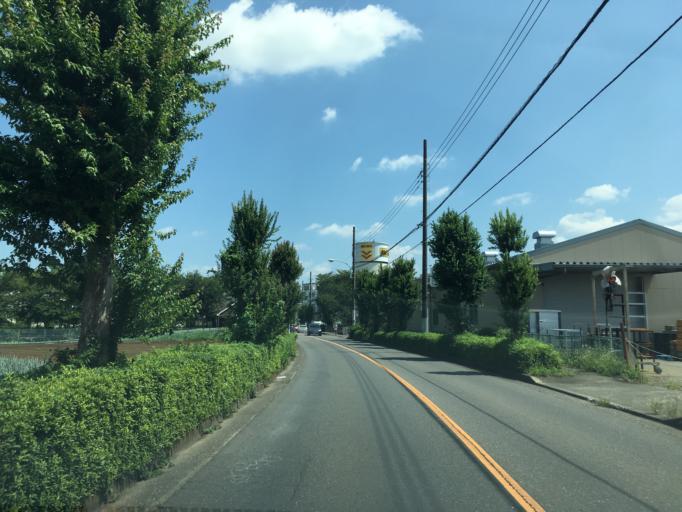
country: JP
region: Tokyo
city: Fussa
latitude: 35.7474
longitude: 139.3790
